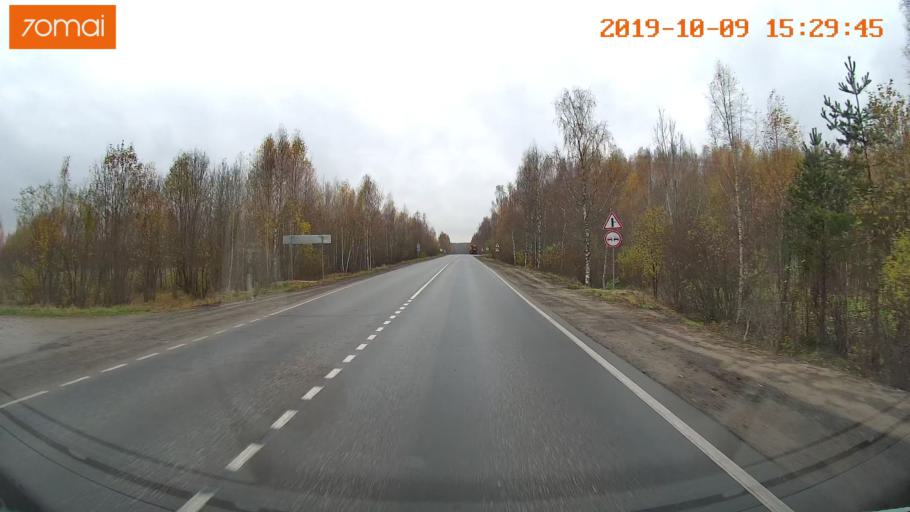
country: RU
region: Kostroma
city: Susanino
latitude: 57.9878
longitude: 41.3375
